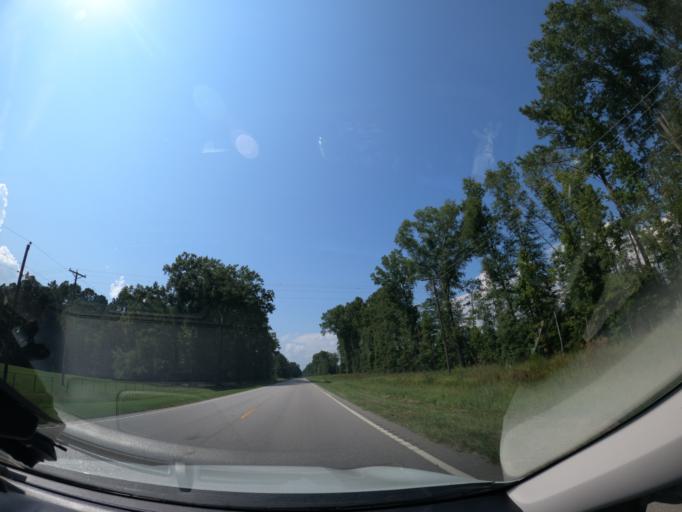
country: US
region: South Carolina
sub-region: Richland County
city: Hopkins
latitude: 33.8890
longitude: -80.9131
